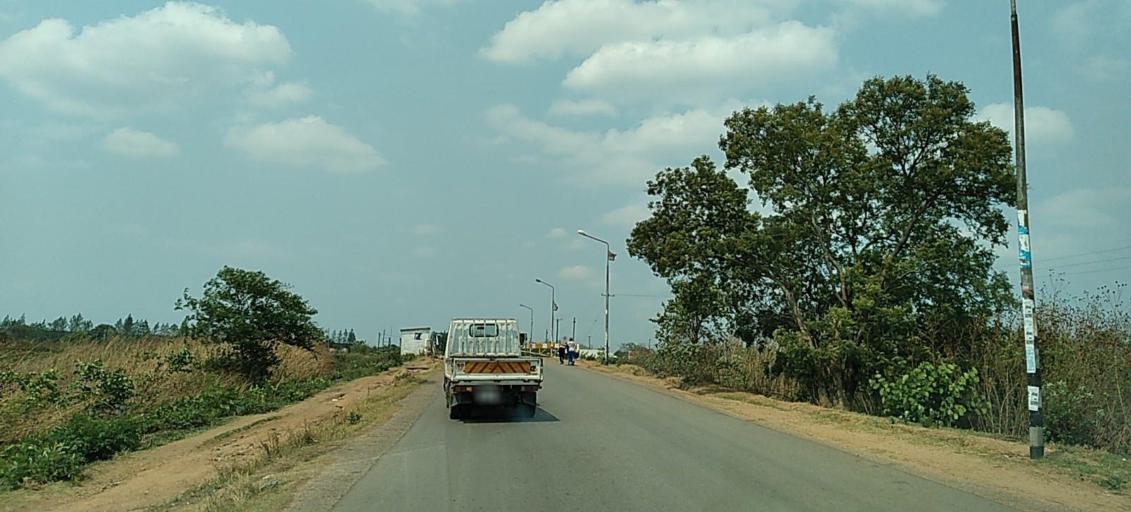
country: ZM
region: Copperbelt
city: Chambishi
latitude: -12.6421
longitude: 28.0574
